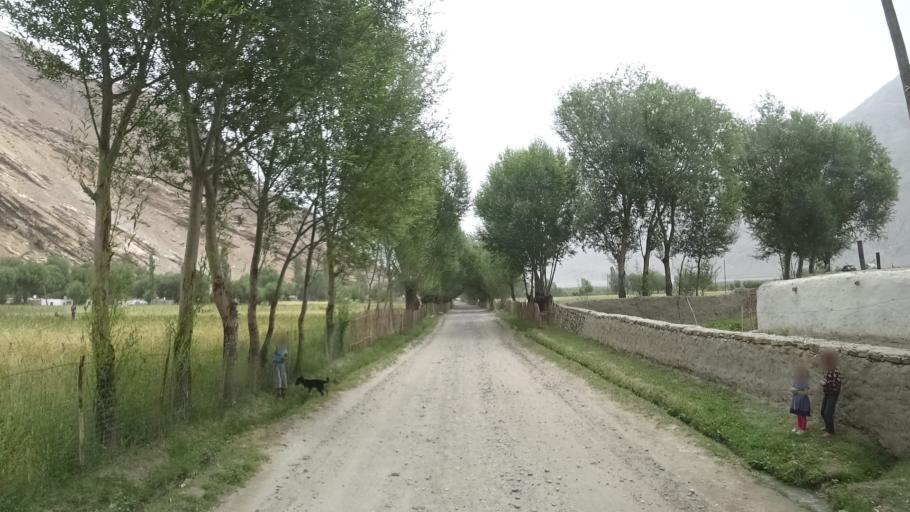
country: AF
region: Badakhshan
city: Khandud
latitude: 37.0221
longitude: 72.5922
